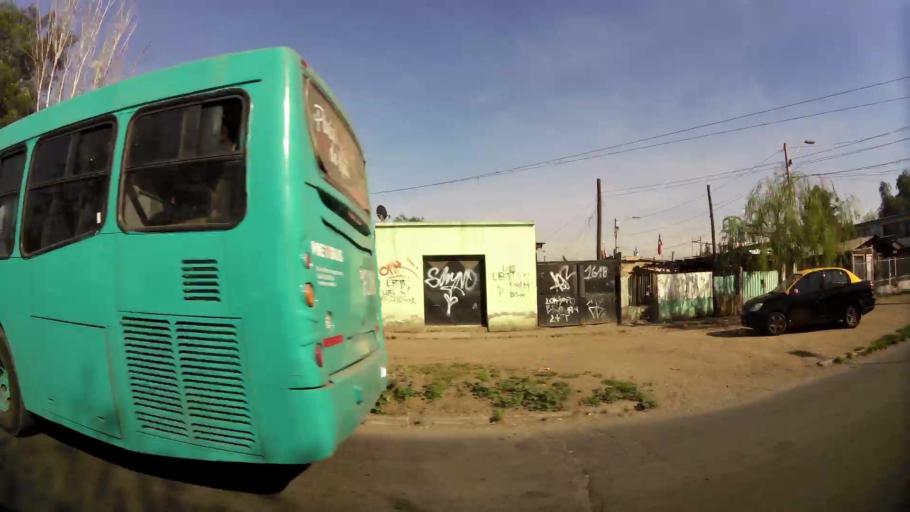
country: CL
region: Santiago Metropolitan
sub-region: Provincia de Santiago
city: Lo Prado
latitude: -33.4267
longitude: -70.7489
